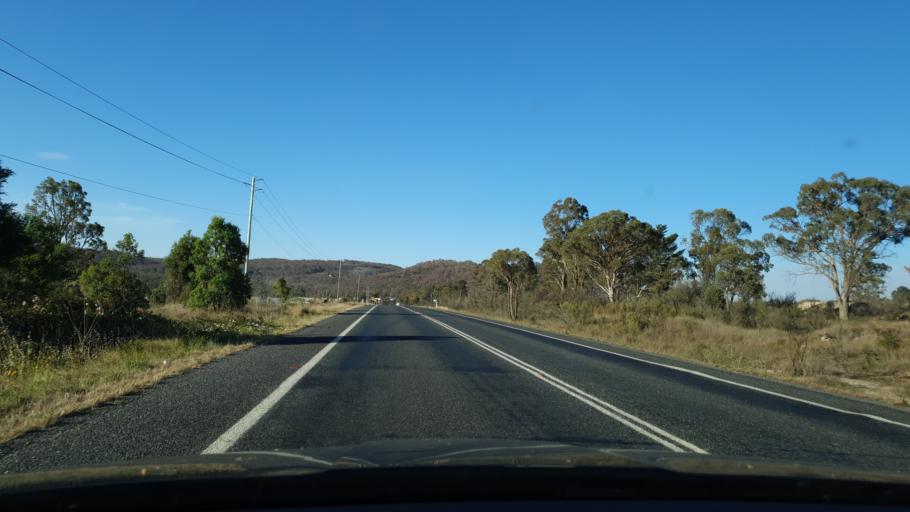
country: AU
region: Queensland
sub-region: Southern Downs
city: Stanthorpe
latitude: -28.6609
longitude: 151.9163
